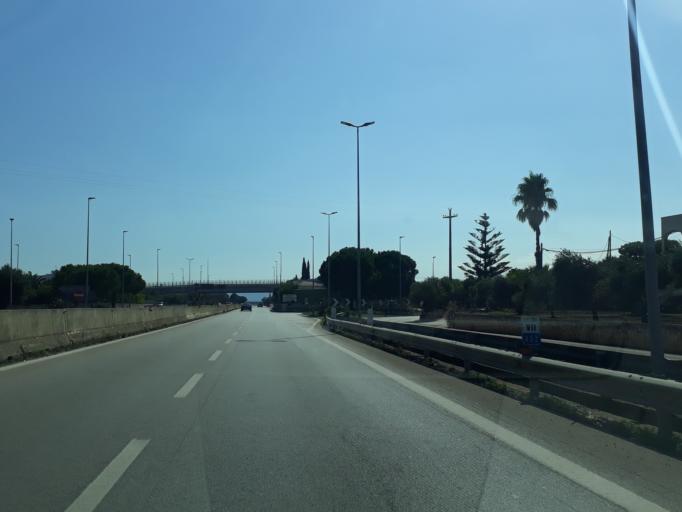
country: IT
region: Apulia
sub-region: Provincia di Brindisi
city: Fasano
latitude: 40.8824
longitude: 17.3371
